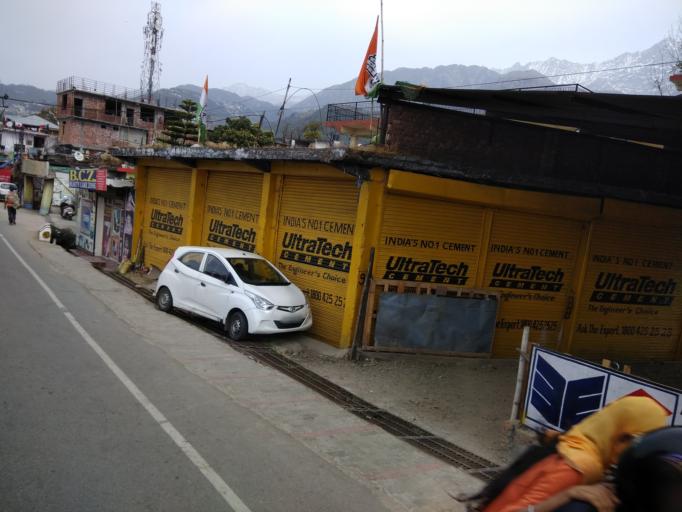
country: IN
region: Himachal Pradesh
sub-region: Kangra
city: Dharmsala
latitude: 32.1993
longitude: 76.3366
